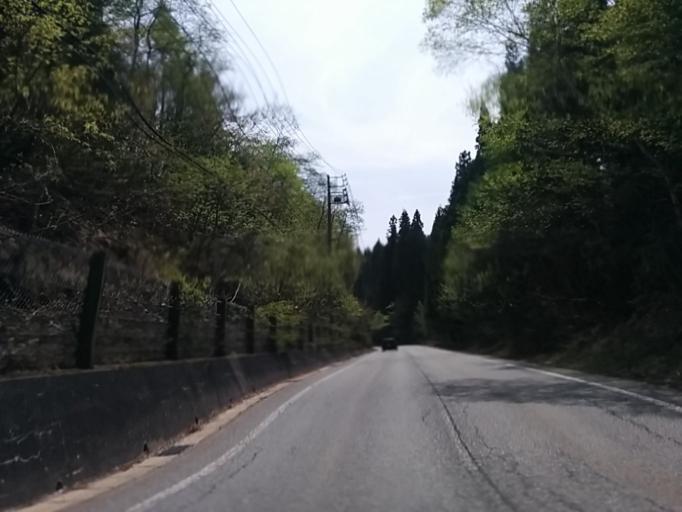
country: JP
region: Gifu
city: Takayama
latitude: 36.2186
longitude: 137.5426
